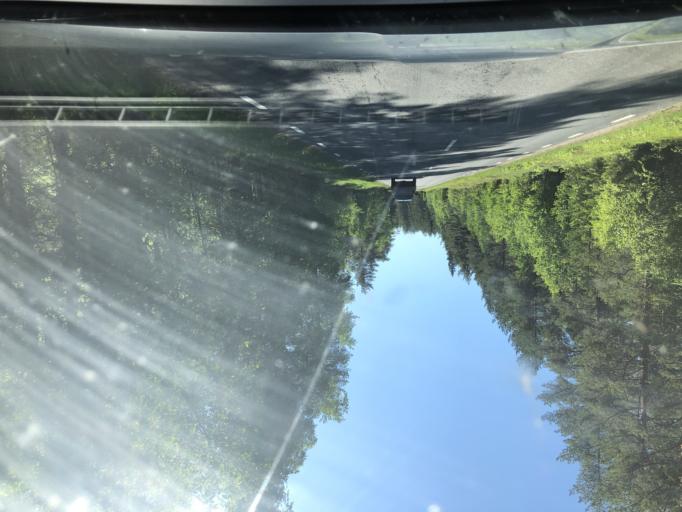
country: SE
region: Norrbotten
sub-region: Lulea Kommun
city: Gammelstad
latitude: 65.6561
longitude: 22.0067
